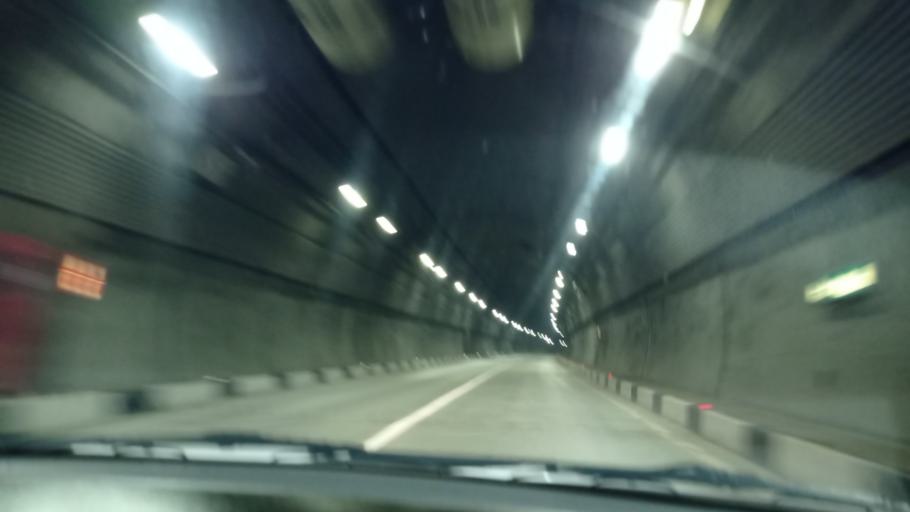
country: RU
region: Krasnodarskiy
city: Vysokoye
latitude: 43.5992
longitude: 40.0251
